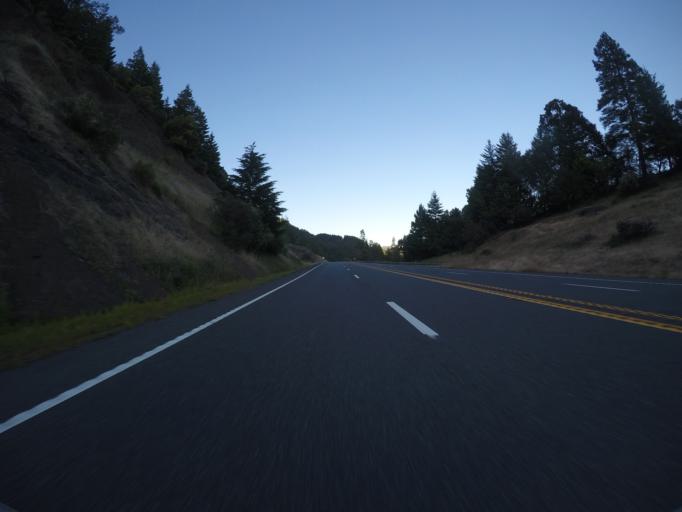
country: US
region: California
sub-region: Mendocino County
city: Laytonville
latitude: 39.8336
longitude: -123.6417
